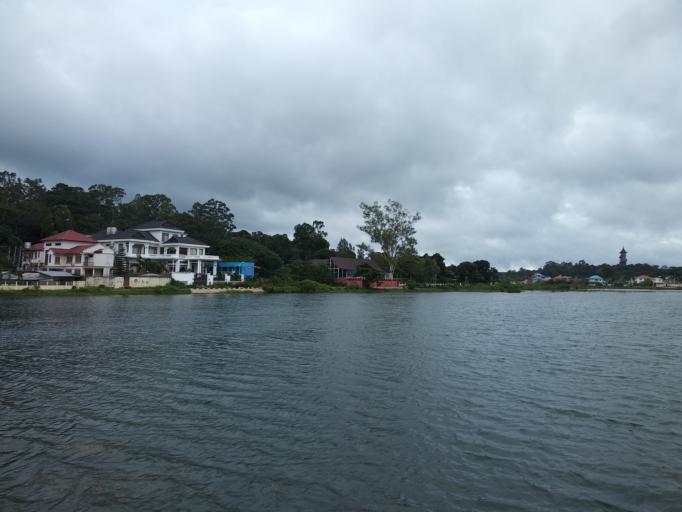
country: MM
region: Mandalay
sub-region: Pyin Oo Lwin District
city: Pyin Oo Lwin
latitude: 22.0139
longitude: 96.4688
